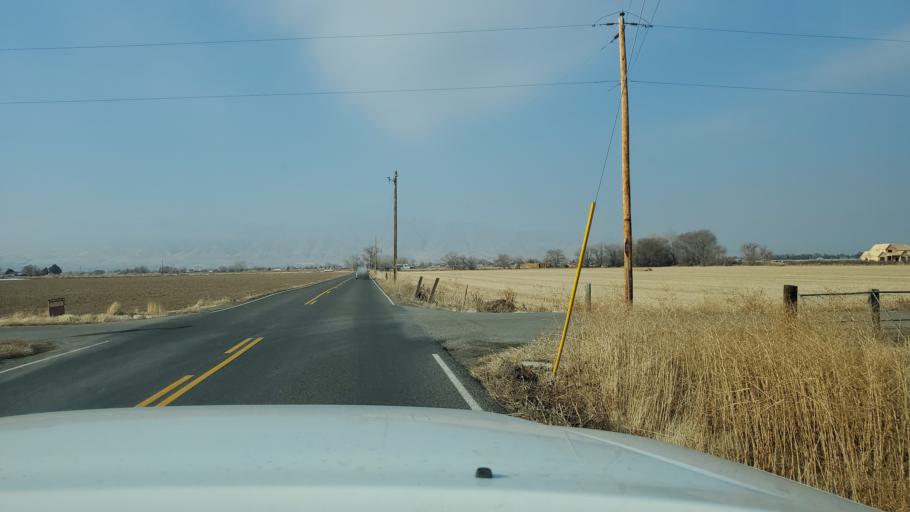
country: US
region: Utah
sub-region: Utah County
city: Benjamin
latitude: 40.0854
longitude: -111.7080
